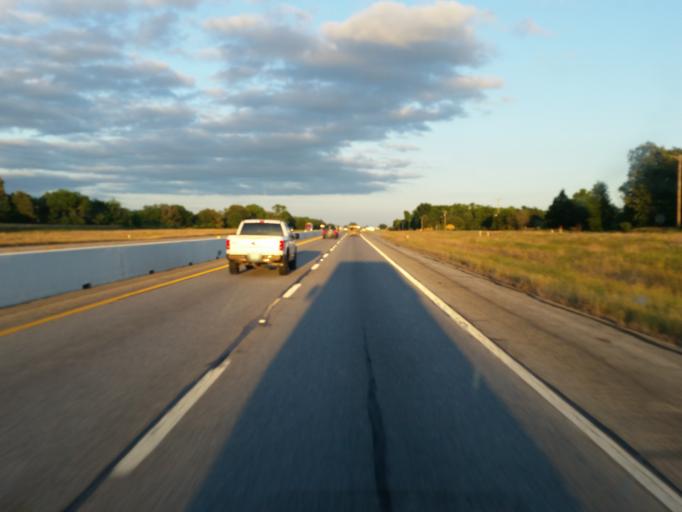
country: US
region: Texas
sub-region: Van Zandt County
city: Van
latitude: 32.5334
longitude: -95.7322
